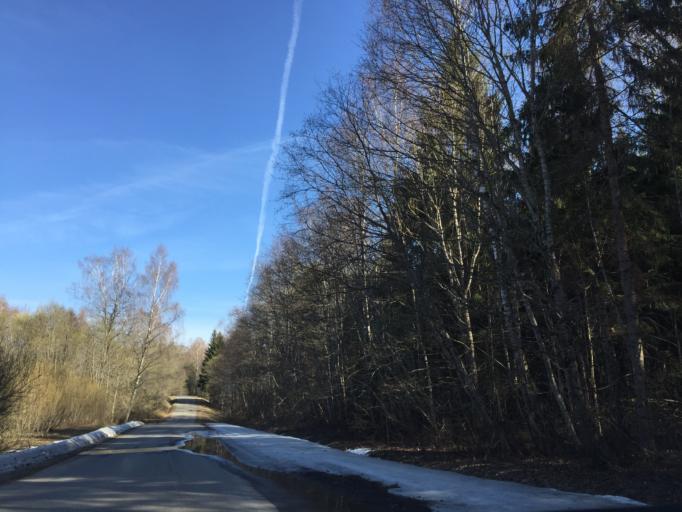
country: EE
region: Vorumaa
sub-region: Antsla vald
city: Vana-Antsla
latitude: 58.0177
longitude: 26.4548
